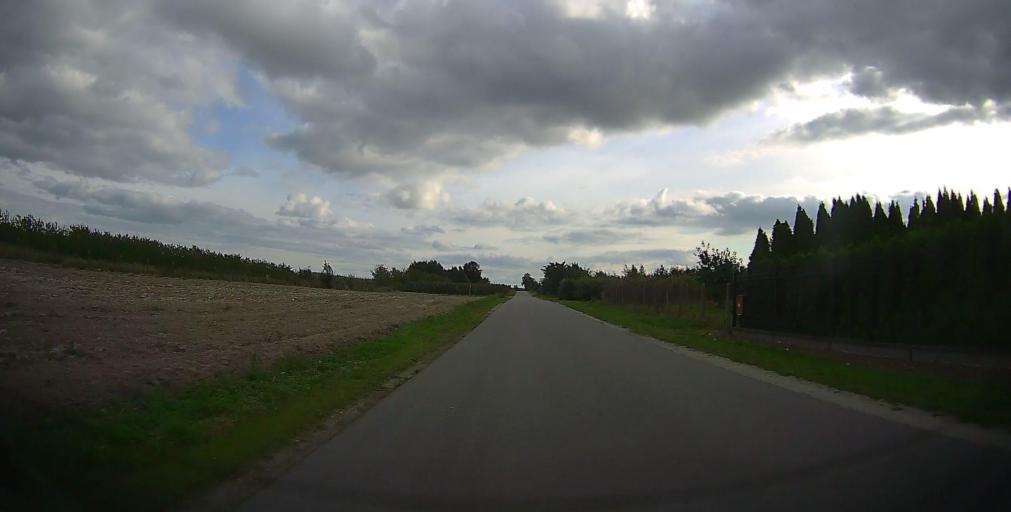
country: PL
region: Masovian Voivodeship
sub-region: Powiat bialobrzeski
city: Promna
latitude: 51.7209
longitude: 20.9586
